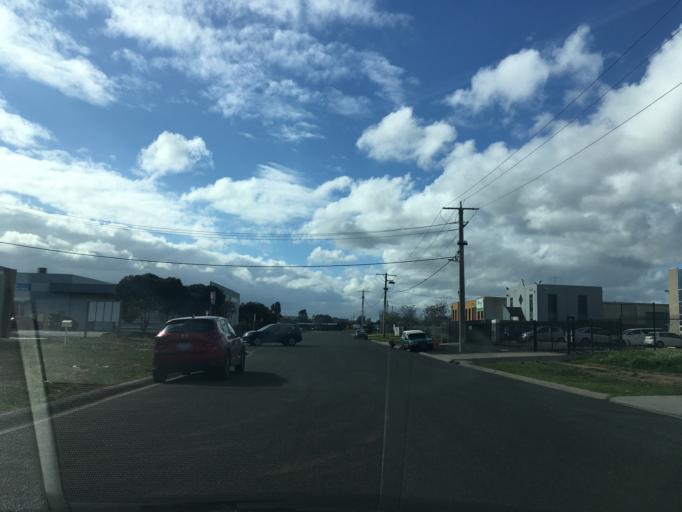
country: AU
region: Victoria
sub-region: Wyndham
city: Williams Landing
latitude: -37.8733
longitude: 144.7295
